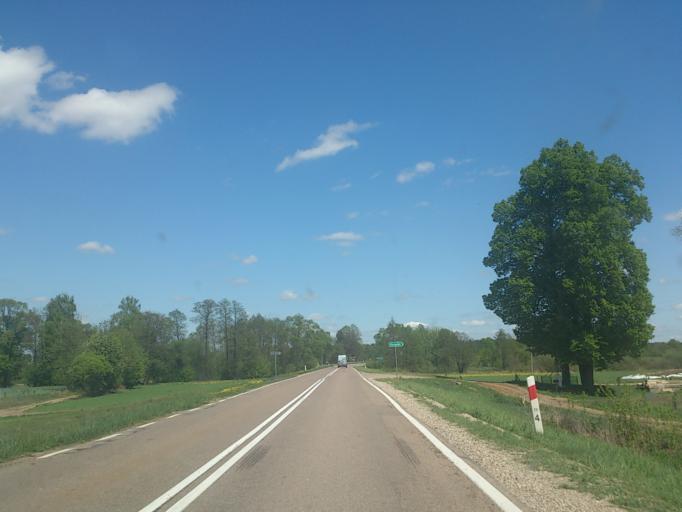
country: PL
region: Podlasie
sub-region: Powiat lomzynski
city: Wizna
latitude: 53.2075
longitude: 22.4902
